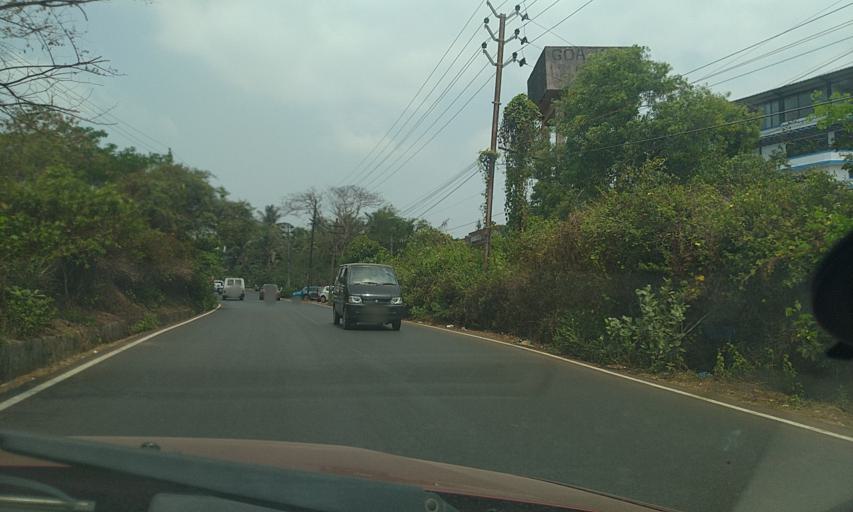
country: IN
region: Goa
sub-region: North Goa
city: Mapuca
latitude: 15.5993
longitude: 73.8092
